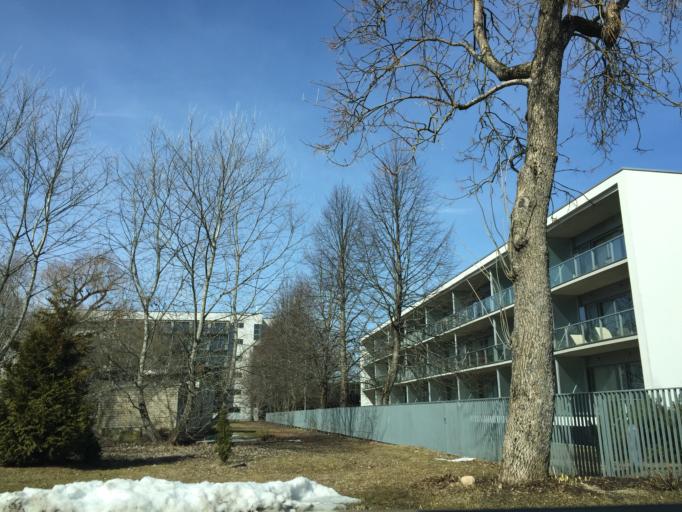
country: EE
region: Paernumaa
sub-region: Paernu linn
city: Parnu
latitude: 58.3814
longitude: 24.4892
